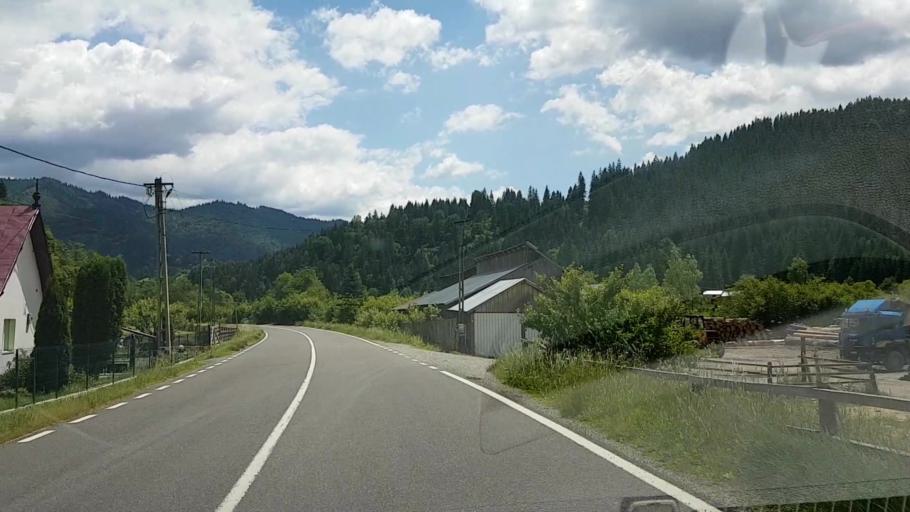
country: RO
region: Suceava
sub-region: Comuna Crucea
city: Crucea
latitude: 47.3950
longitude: 25.5642
